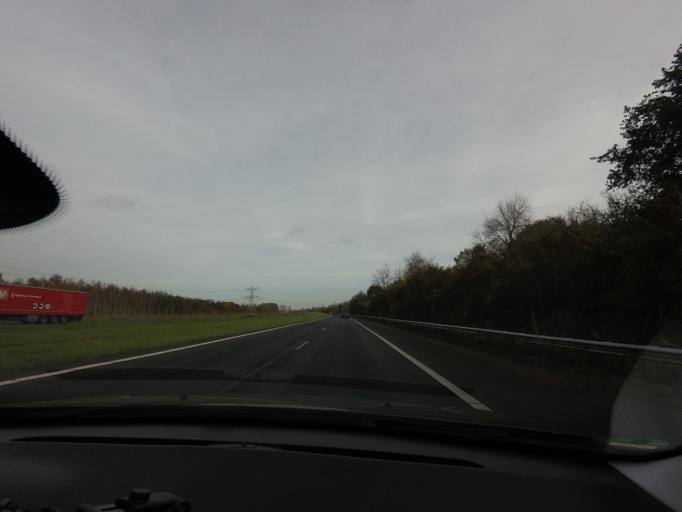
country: NL
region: Flevoland
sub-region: Gemeente Lelystad
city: Lelystad
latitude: 52.4926
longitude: 5.5242
